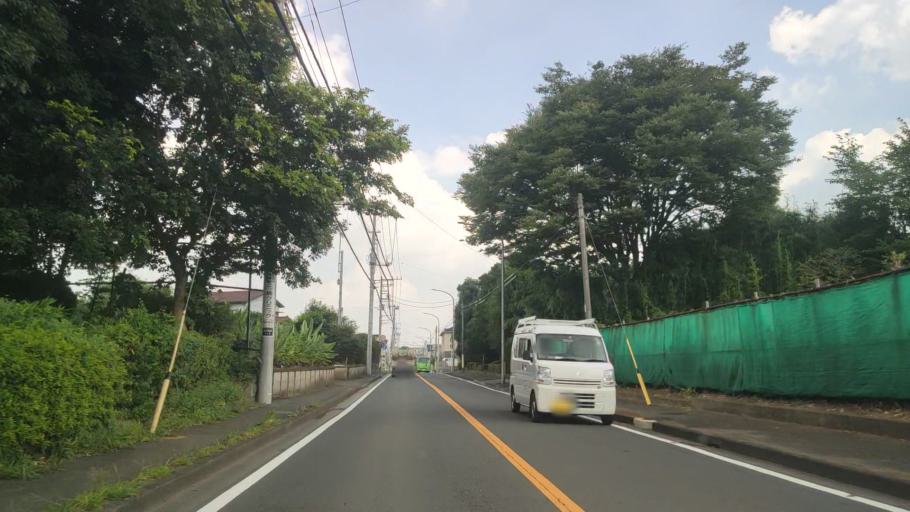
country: JP
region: Kanagawa
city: Minami-rinkan
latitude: 35.4546
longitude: 139.5017
